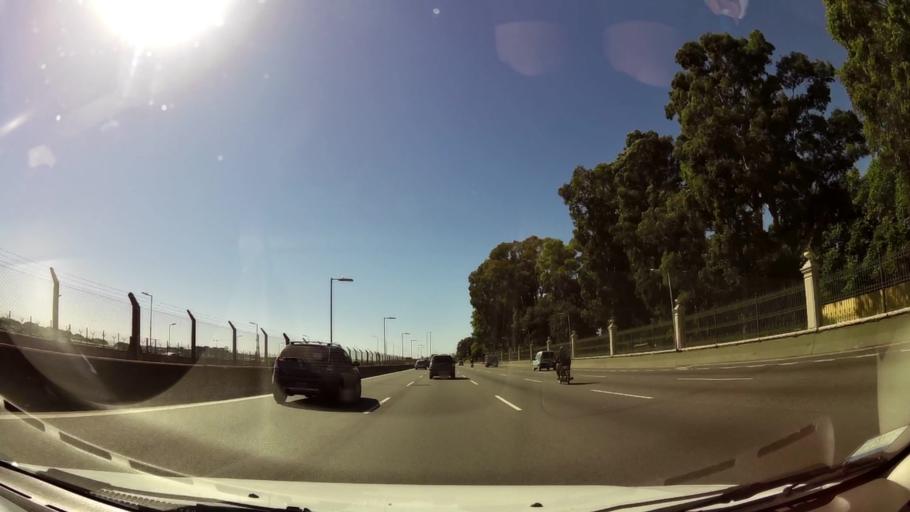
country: AR
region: Buenos Aires F.D.
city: Colegiales
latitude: -34.5556
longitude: -58.4260
